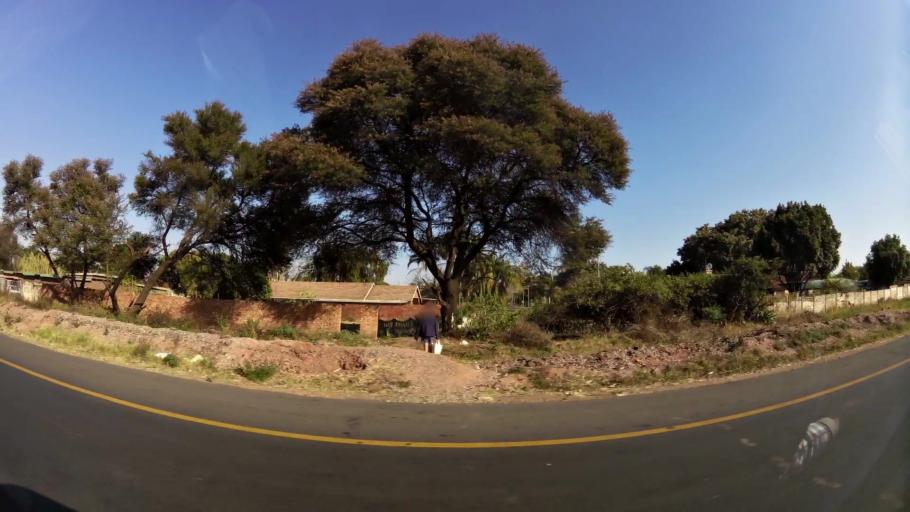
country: ZA
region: Gauteng
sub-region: City of Tshwane Metropolitan Municipality
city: Pretoria
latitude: -25.7048
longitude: 28.1565
